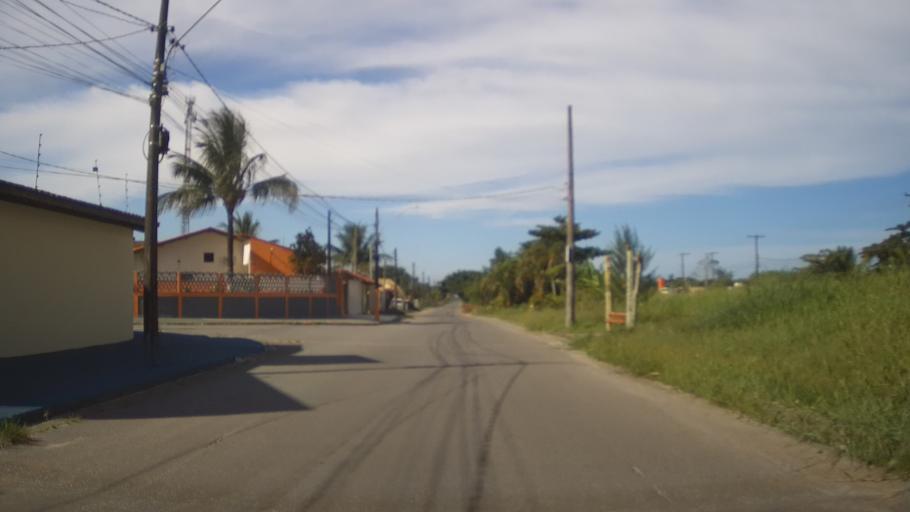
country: BR
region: Sao Paulo
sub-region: Itanhaem
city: Itanhaem
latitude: -24.2172
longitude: -46.8570
